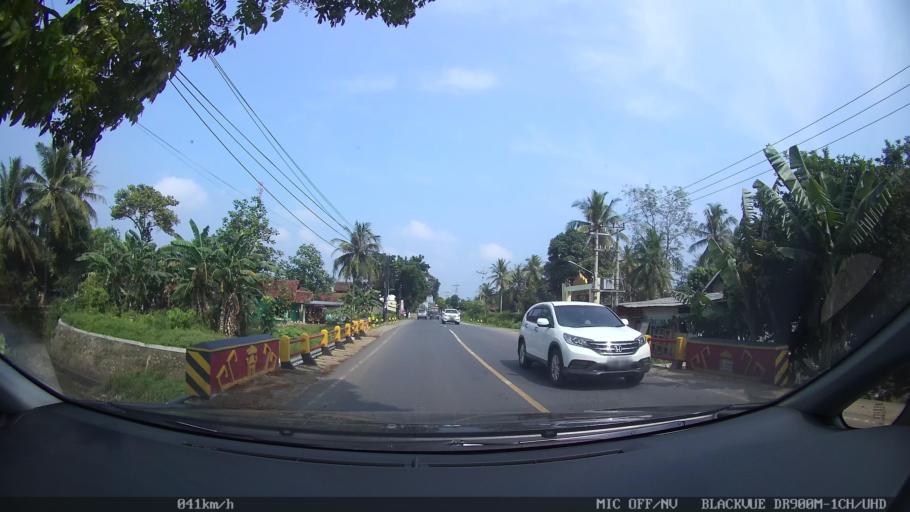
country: ID
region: Lampung
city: Gadingrejo
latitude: -5.3723
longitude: 105.0771
